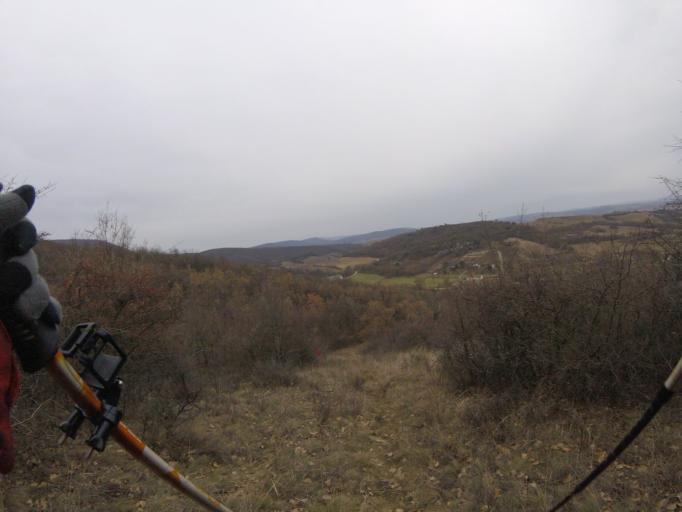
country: HU
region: Komarom-Esztergom
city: Kesztolc
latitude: 47.7163
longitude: 18.8135
